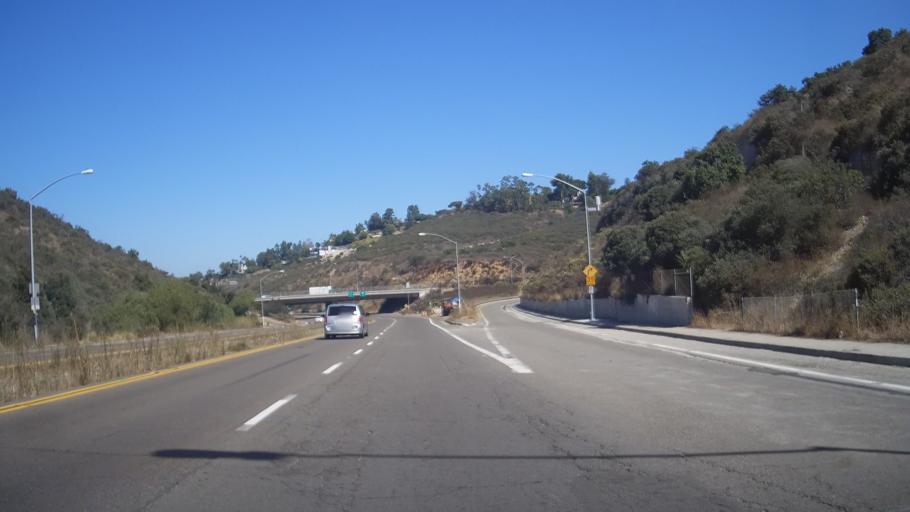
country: US
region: California
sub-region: San Diego County
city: Lemon Grove
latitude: 32.7699
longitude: -117.0968
